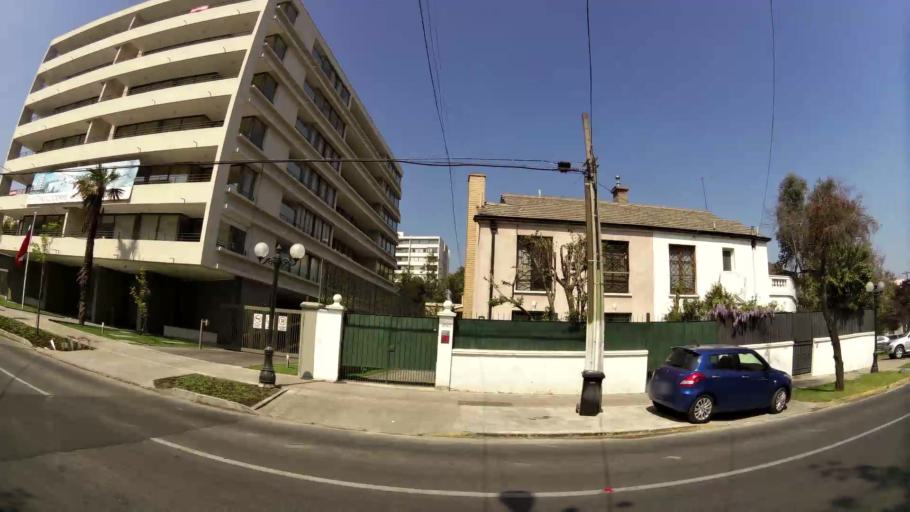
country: CL
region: Santiago Metropolitan
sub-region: Provincia de Santiago
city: Villa Presidente Frei, Nunoa, Santiago, Chile
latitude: -33.4433
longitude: -70.6041
